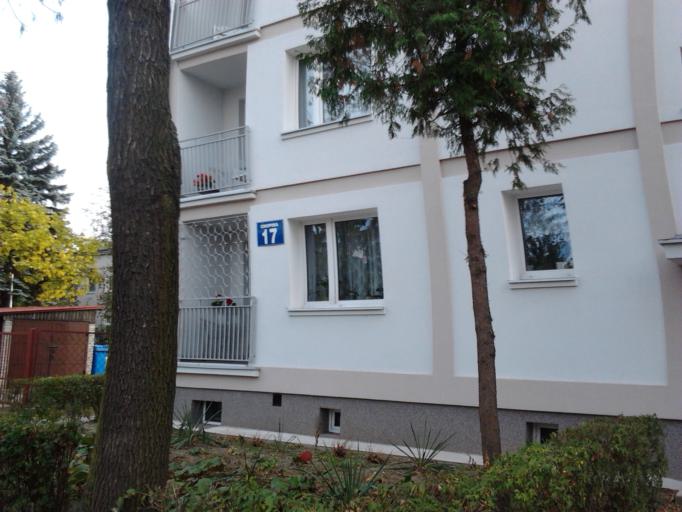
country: PL
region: Masovian Voivodeship
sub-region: Powiat pruszkowski
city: Pruszkow
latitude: 52.1620
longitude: 20.7981
